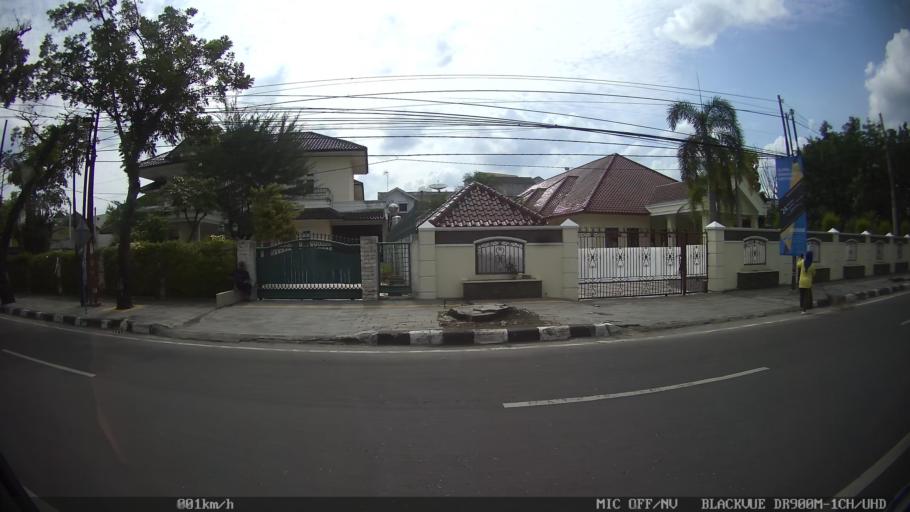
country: ID
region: North Sumatra
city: Medan
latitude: 3.5788
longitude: 98.6672
